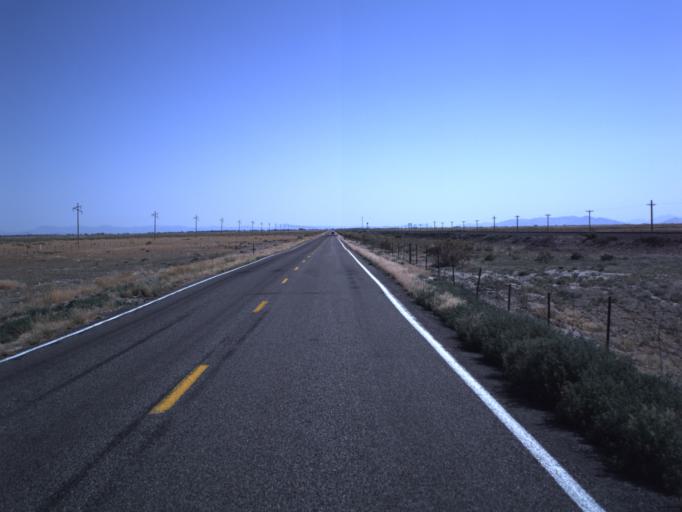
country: US
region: Utah
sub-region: Millard County
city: Delta
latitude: 39.1906
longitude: -112.6939
